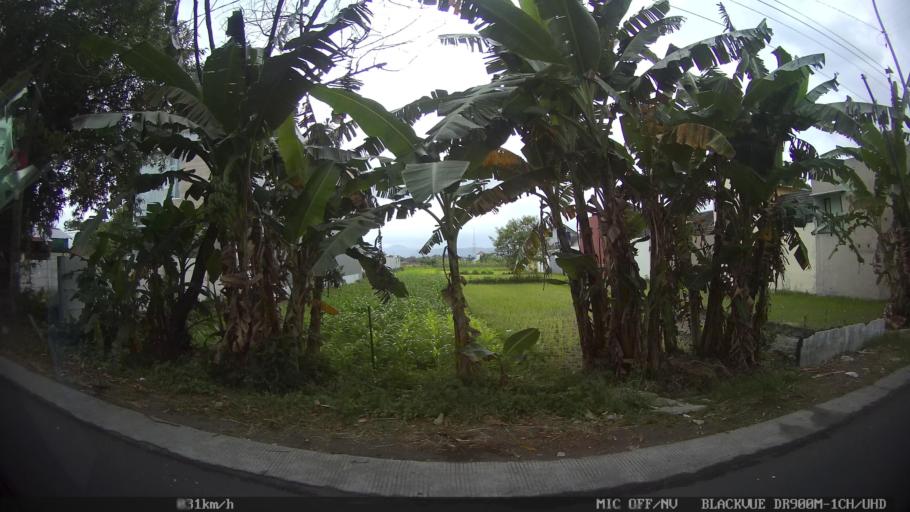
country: ID
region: Daerah Istimewa Yogyakarta
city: Depok
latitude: -7.8256
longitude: 110.4140
